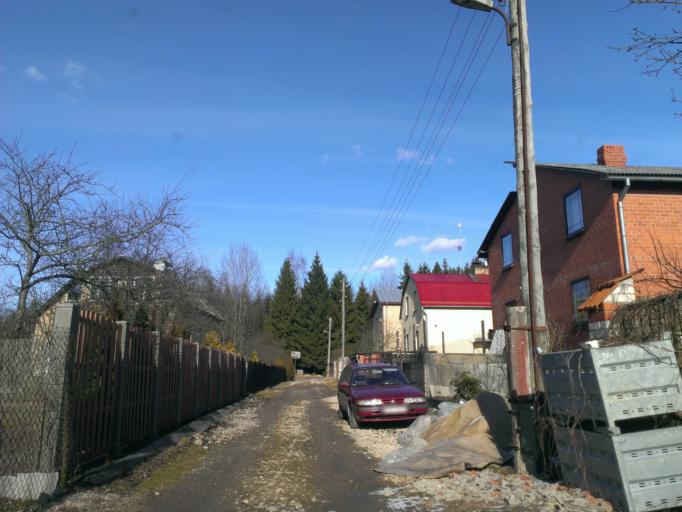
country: LV
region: Garkalne
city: Garkalne
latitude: 56.9502
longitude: 24.4533
